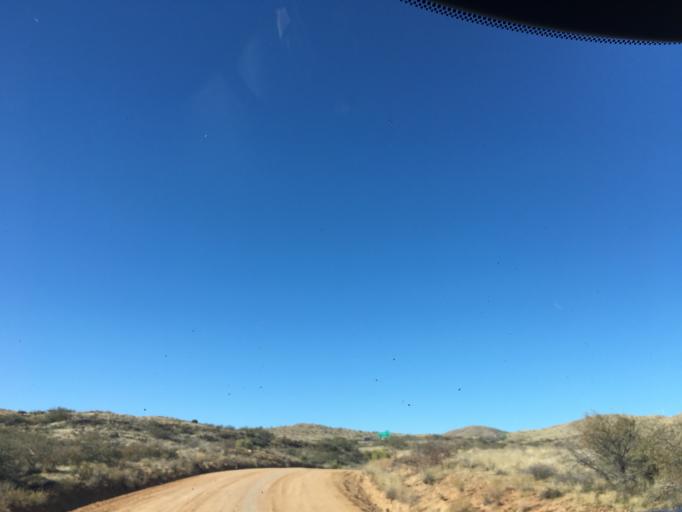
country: US
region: Arizona
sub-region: Yavapai County
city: Cordes Lakes
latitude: 34.2712
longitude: -112.1106
